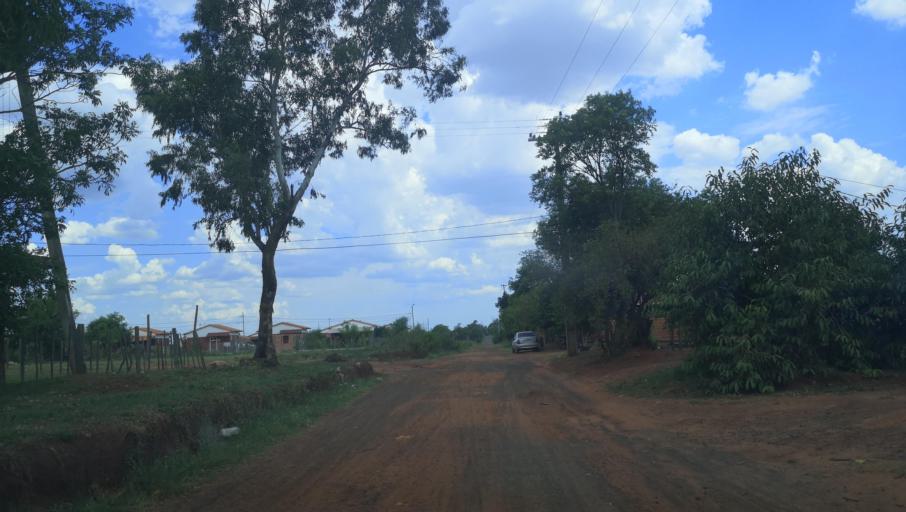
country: PY
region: Misiones
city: Santa Maria
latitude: -26.9011
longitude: -57.0392
